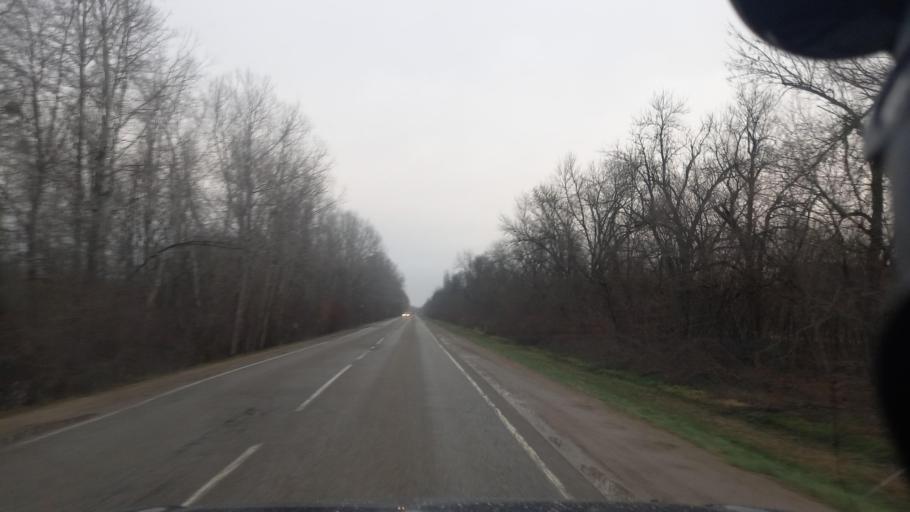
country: RU
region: Krasnodarskiy
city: Saratovskaya
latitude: 44.6812
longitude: 39.2099
